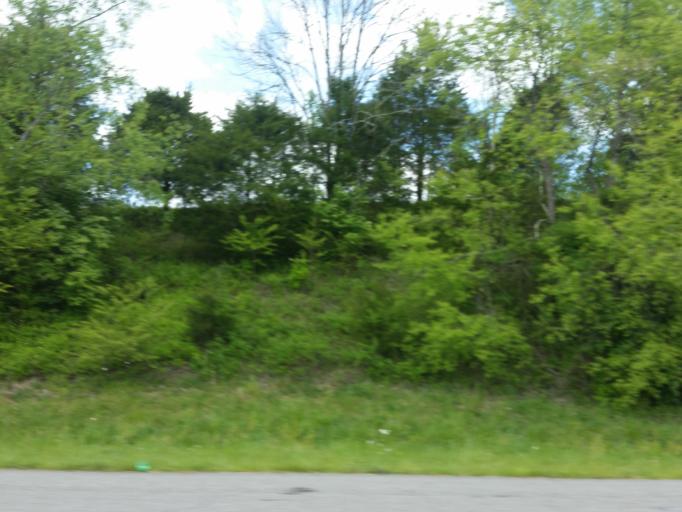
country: US
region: Tennessee
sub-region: Campbell County
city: Fincastle
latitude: 36.4440
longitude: -83.9873
